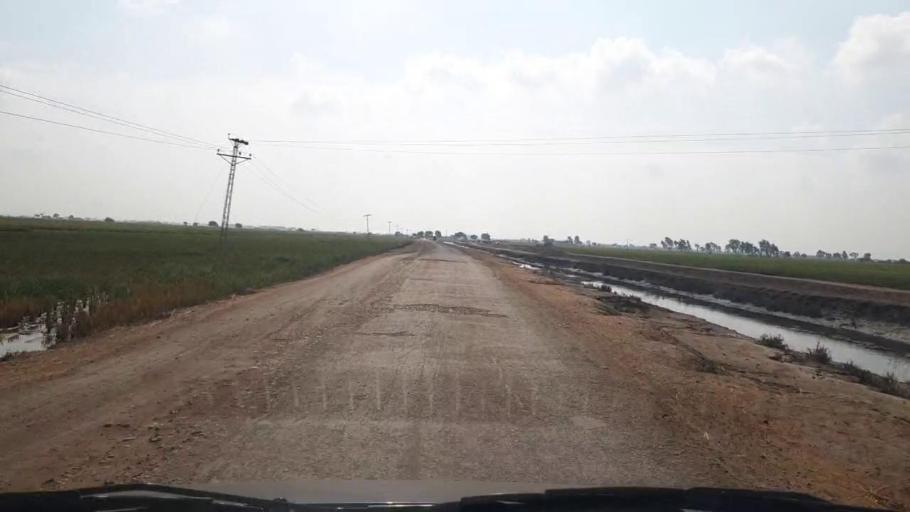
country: PK
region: Sindh
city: Kario
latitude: 24.6232
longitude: 68.5552
